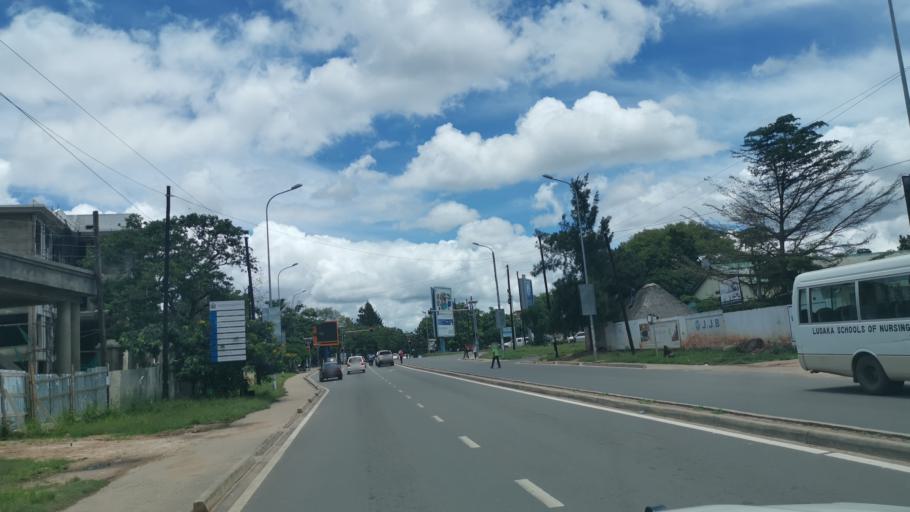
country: ZM
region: Lusaka
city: Lusaka
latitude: -15.4261
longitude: 28.3119
